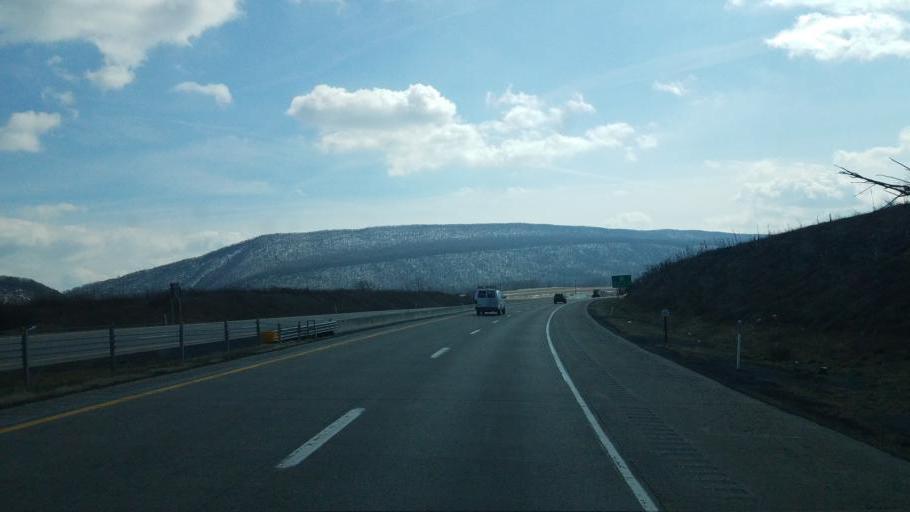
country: US
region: Pennsylvania
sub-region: Mifflin County
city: Church Hill
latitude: 40.6745
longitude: -77.6036
